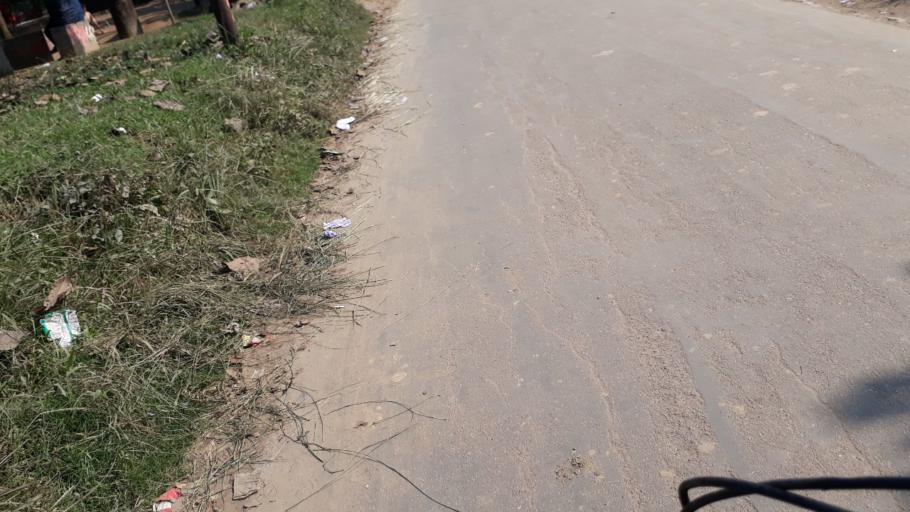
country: BD
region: Dhaka
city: Tungi
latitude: 23.8799
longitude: 90.2650
